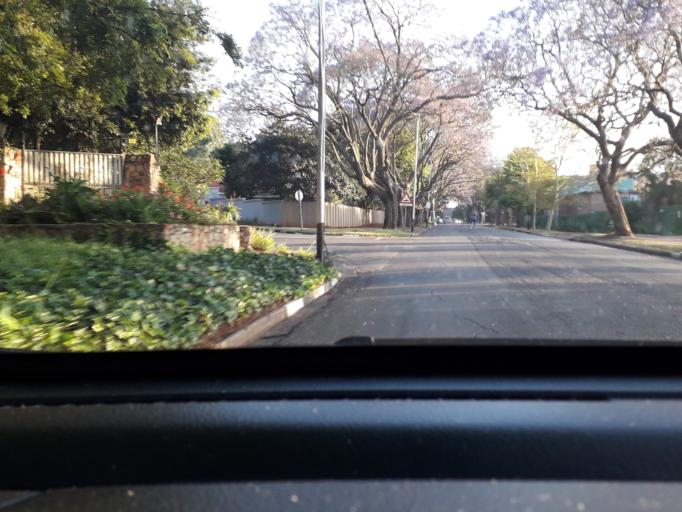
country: ZA
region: Gauteng
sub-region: City of Johannesburg Metropolitan Municipality
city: Johannesburg
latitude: -26.1389
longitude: 28.0527
